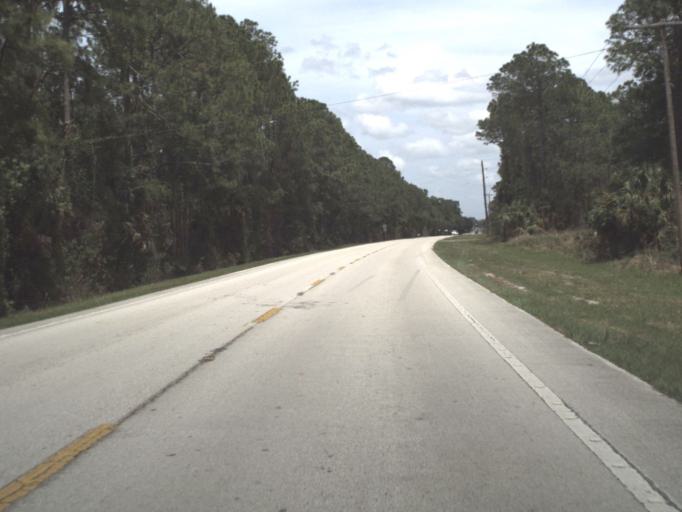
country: US
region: Florida
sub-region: Lake County
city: Lake Mack-Forest Hills
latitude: 29.0004
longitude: -81.3914
